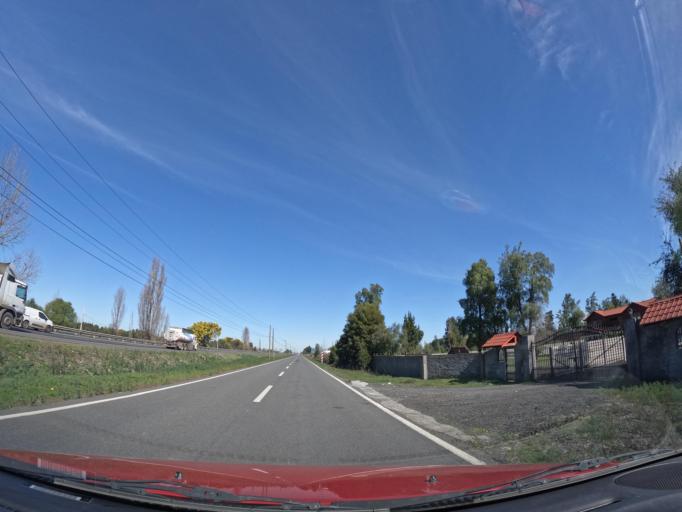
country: CL
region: Biobio
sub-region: Provincia de Biobio
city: Cabrero
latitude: -37.0214
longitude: -72.3670
